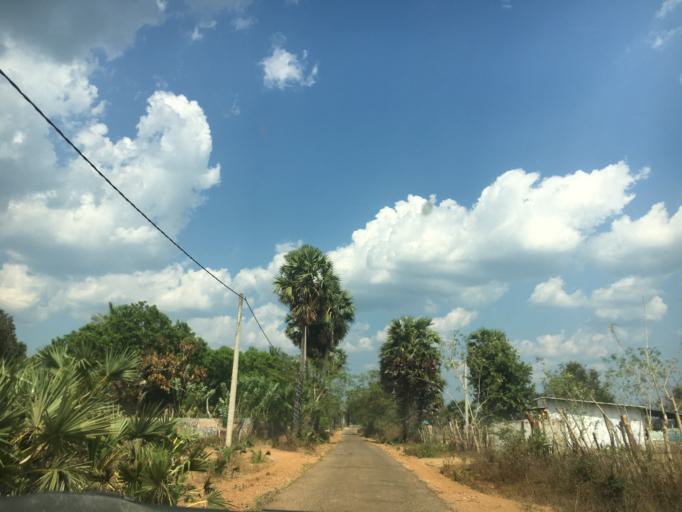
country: LK
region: Northern Province
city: Kilinochchi
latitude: 9.1391
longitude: 80.4497
